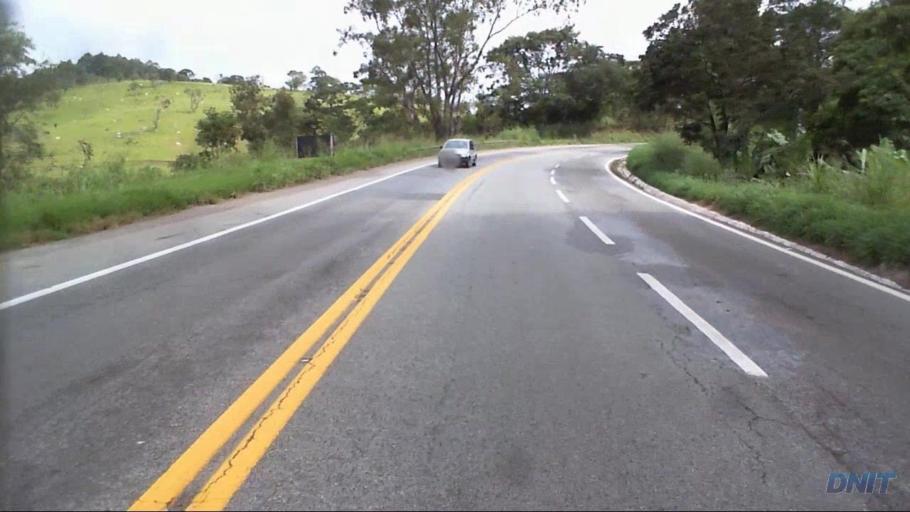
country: BR
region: Minas Gerais
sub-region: Caete
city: Caete
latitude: -19.7232
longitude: -43.5786
